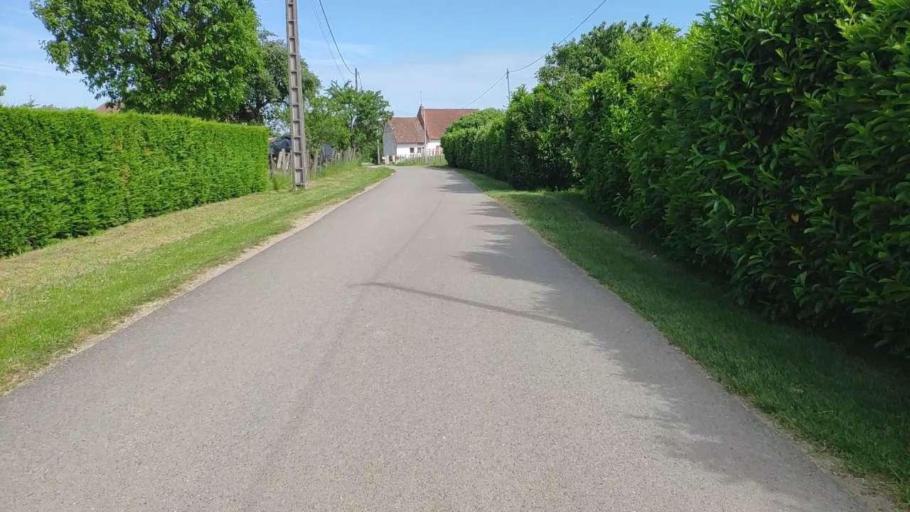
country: FR
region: Franche-Comte
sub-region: Departement du Jura
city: Bletterans
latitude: 46.7126
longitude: 5.4657
